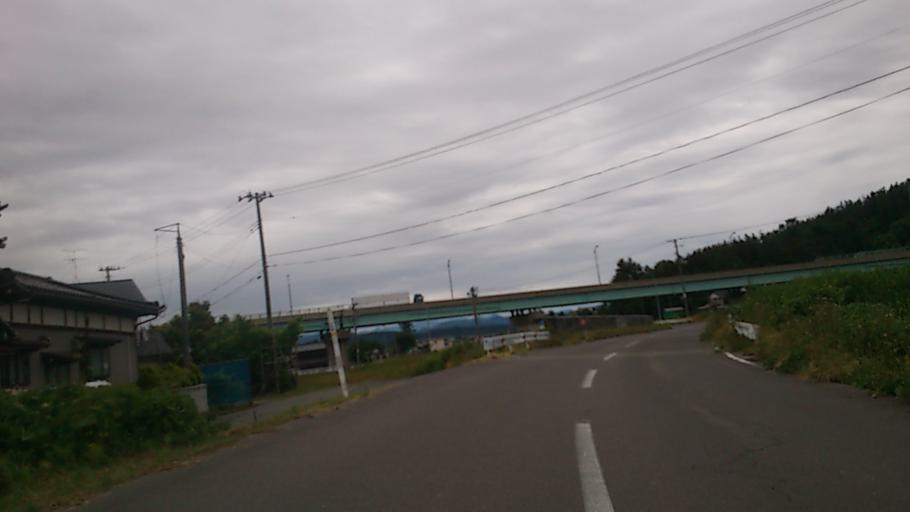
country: JP
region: Yamagata
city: Yuza
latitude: 39.0683
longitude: 139.8806
